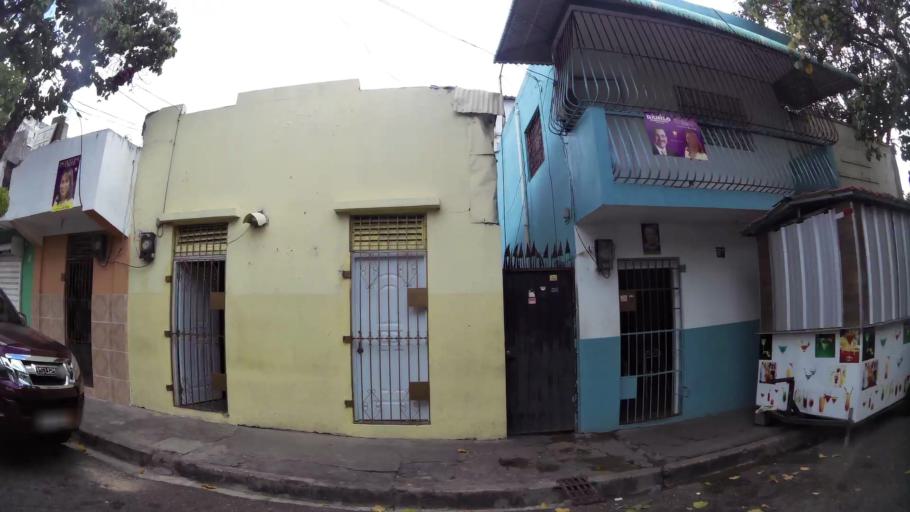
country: DO
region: Nacional
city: San Carlos
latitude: 18.4783
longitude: -69.8964
